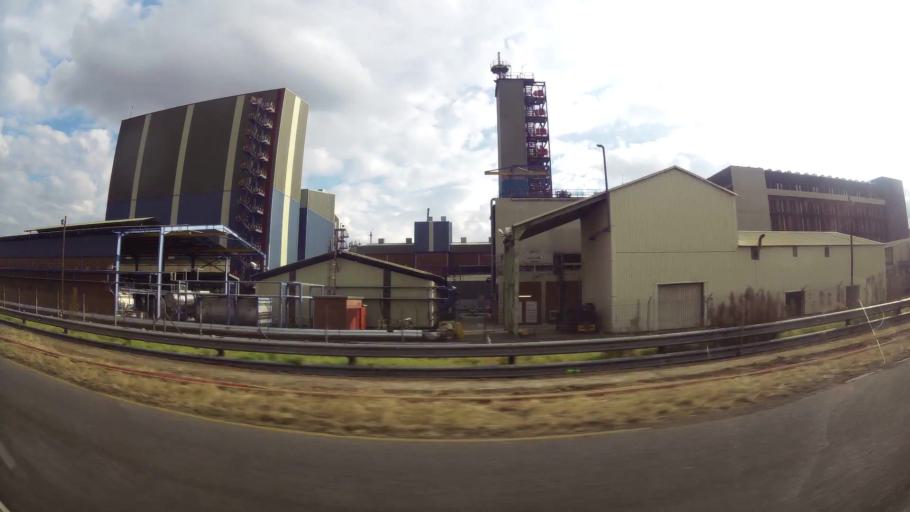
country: ZA
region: Orange Free State
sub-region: Fezile Dabi District Municipality
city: Sasolburg
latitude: -26.8212
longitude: 27.8450
